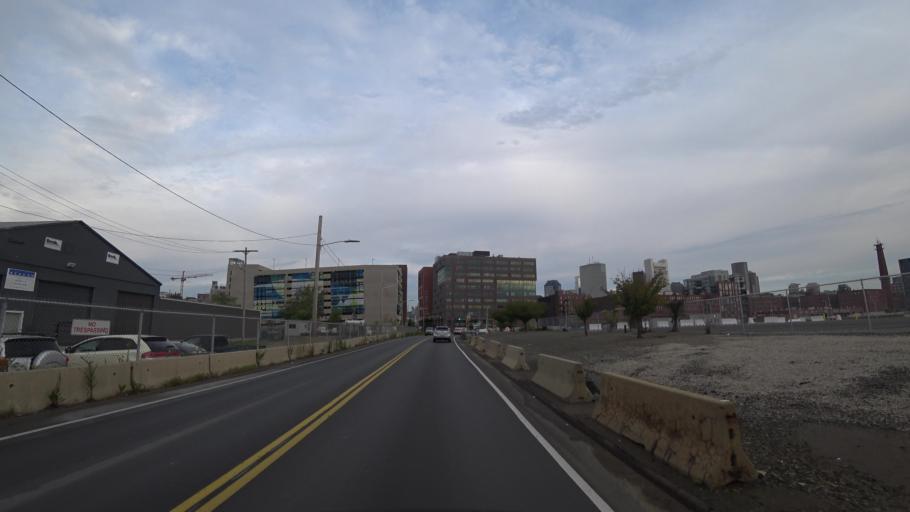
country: US
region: Massachusetts
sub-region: Suffolk County
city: South Boston
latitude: 42.3426
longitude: -71.0498
